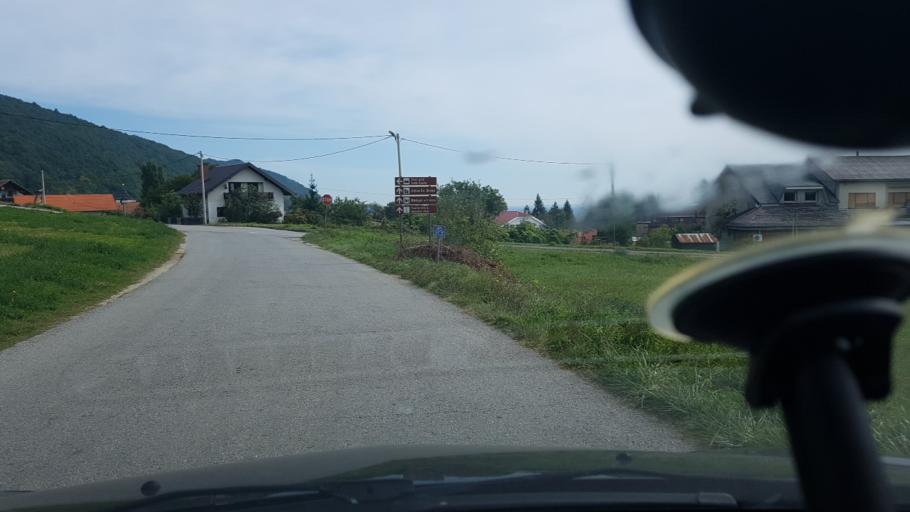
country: HR
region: Varazdinska
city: Ljubescica
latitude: 46.1265
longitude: 16.4610
